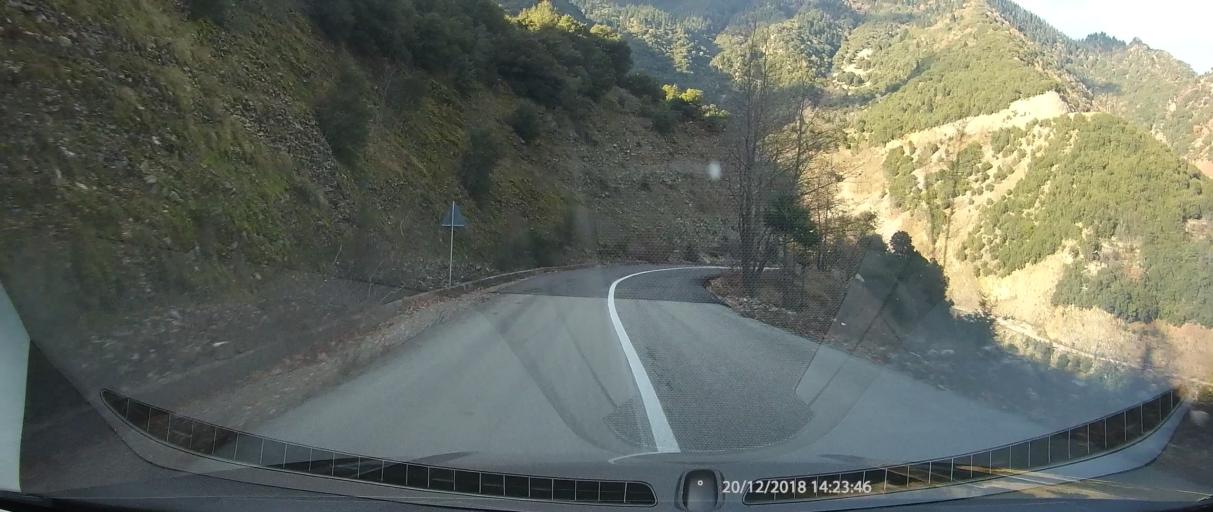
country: GR
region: West Greece
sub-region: Nomos Aitolias kai Akarnanias
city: Thermo
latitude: 38.7576
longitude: 21.6701
